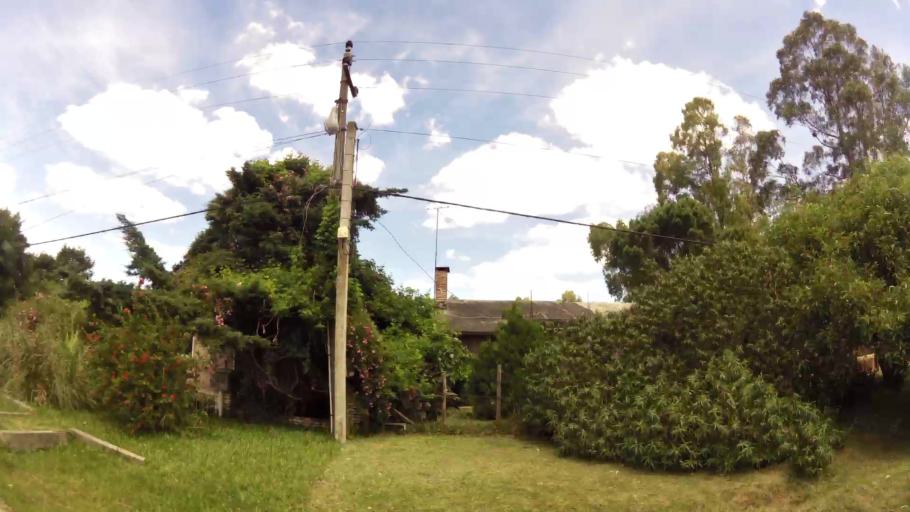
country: UY
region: Canelones
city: Empalme Olmos
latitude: -34.7768
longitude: -55.8862
